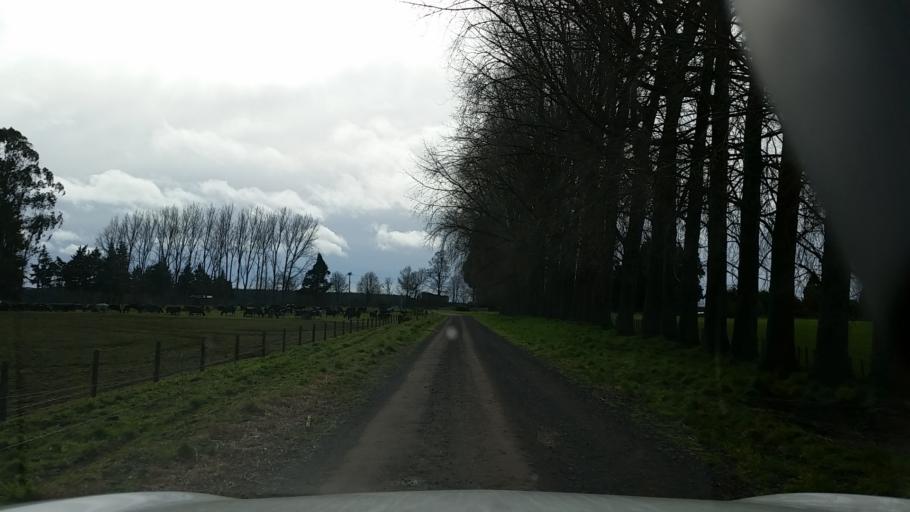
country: NZ
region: Bay of Plenty
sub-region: Whakatane District
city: Murupara
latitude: -38.4698
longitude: 176.4171
